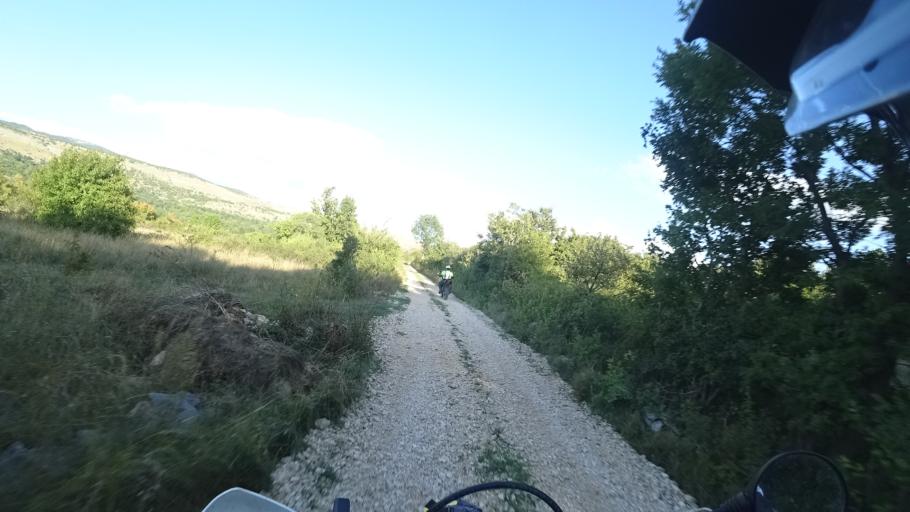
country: HR
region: Sibensko-Kniniska
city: Knin
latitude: 44.1653
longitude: 16.0867
